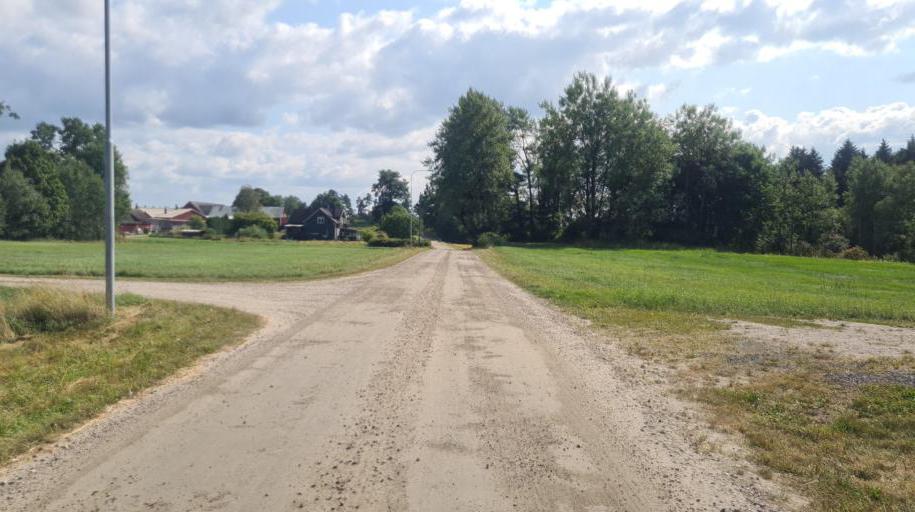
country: SE
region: Kronoberg
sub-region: Ljungby Kommun
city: Ljungby
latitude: 56.7353
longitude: 13.8722
